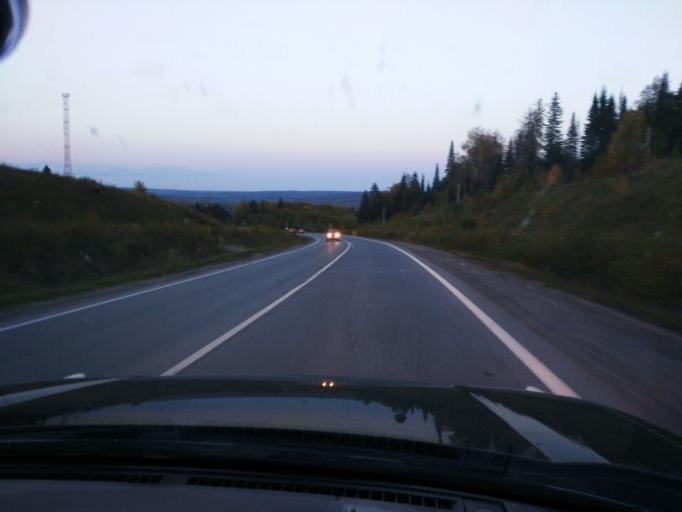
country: RU
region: Perm
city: Sylva
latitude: 58.2915
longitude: 56.8260
